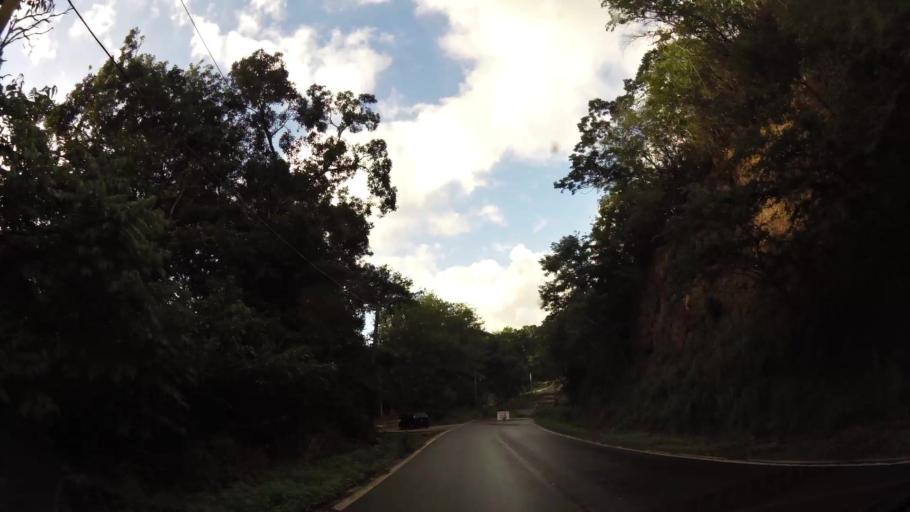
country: DM
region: Saint Peter
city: Colihaut
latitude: 15.5326
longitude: -61.4745
